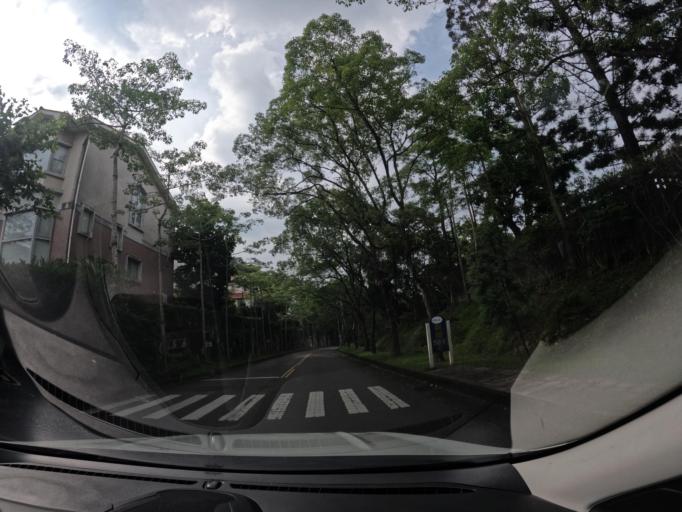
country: TW
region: Taiwan
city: Daxi
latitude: 24.8906
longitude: 121.3228
